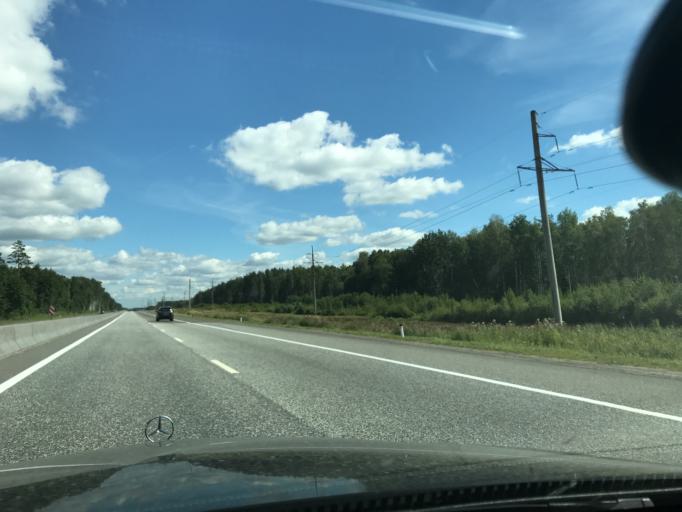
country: RU
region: Nizjnij Novgorod
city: Novosmolinskiy
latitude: 56.2800
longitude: 43.0548
